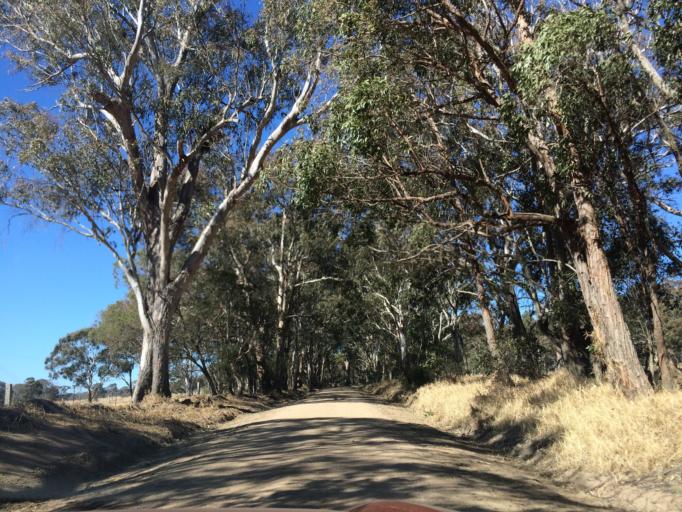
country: AU
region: Queensland
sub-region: Southern Downs
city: Stanthorpe
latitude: -28.6545
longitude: 152.0849
